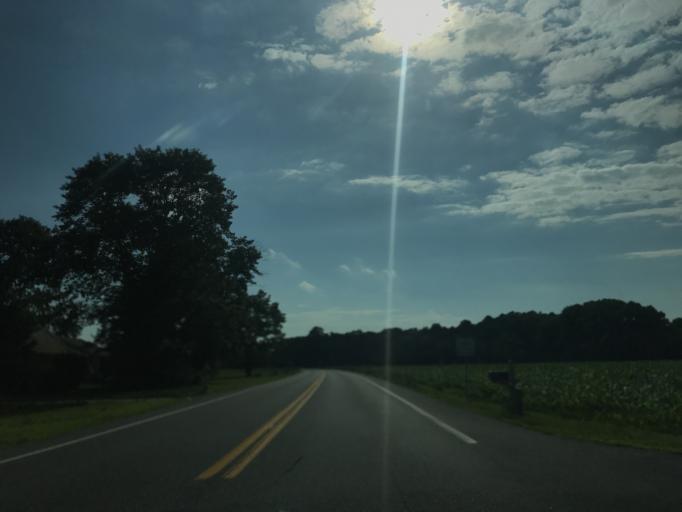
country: US
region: Maryland
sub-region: Wicomico County
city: Hebron
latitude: 38.4654
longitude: -75.7203
